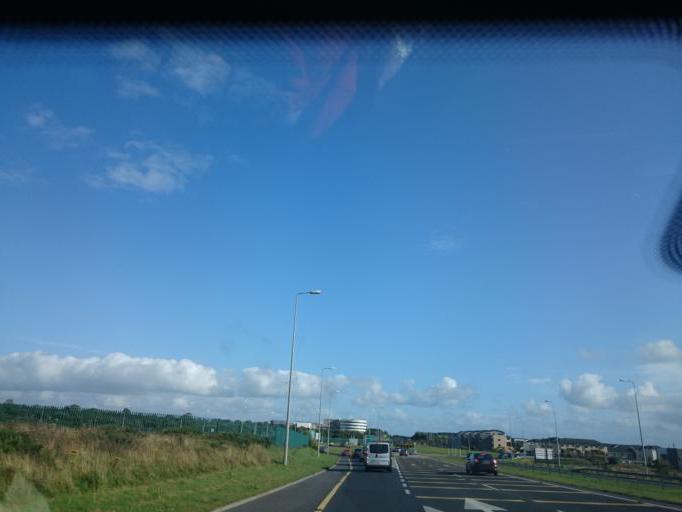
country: IE
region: Connaught
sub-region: County Galway
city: Claregalway
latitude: 53.2870
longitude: -8.9808
